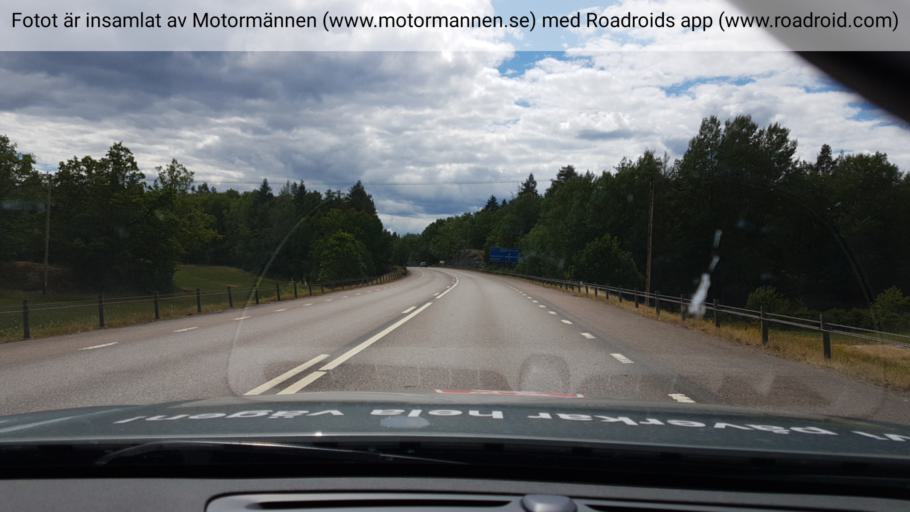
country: SE
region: Kalmar
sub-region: Vasterviks Kommun
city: Ankarsrum
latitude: 57.5768
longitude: 16.4834
